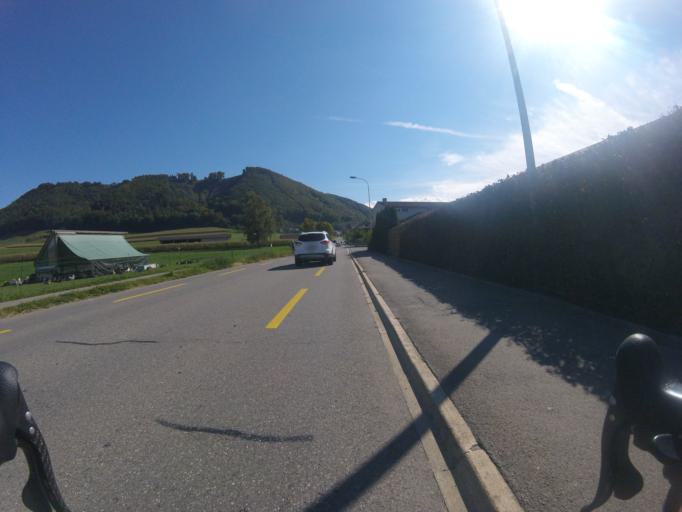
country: CH
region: Bern
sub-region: Bern-Mittelland District
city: Belp
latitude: 46.8861
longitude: 7.5038
